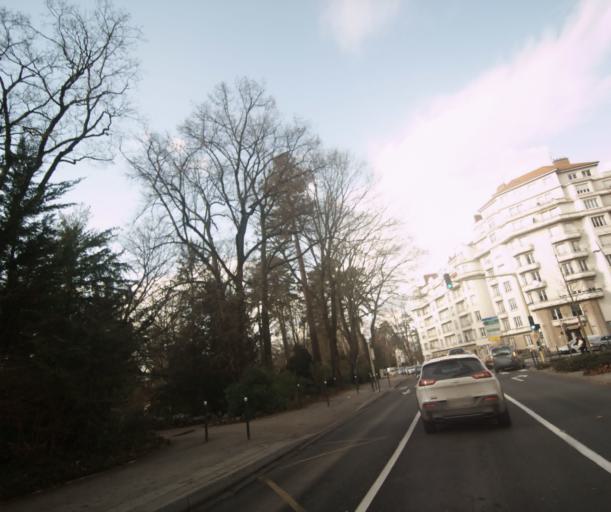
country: FR
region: Franche-Comte
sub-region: Departement du Doubs
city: Besancon
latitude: 47.2412
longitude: 6.0330
